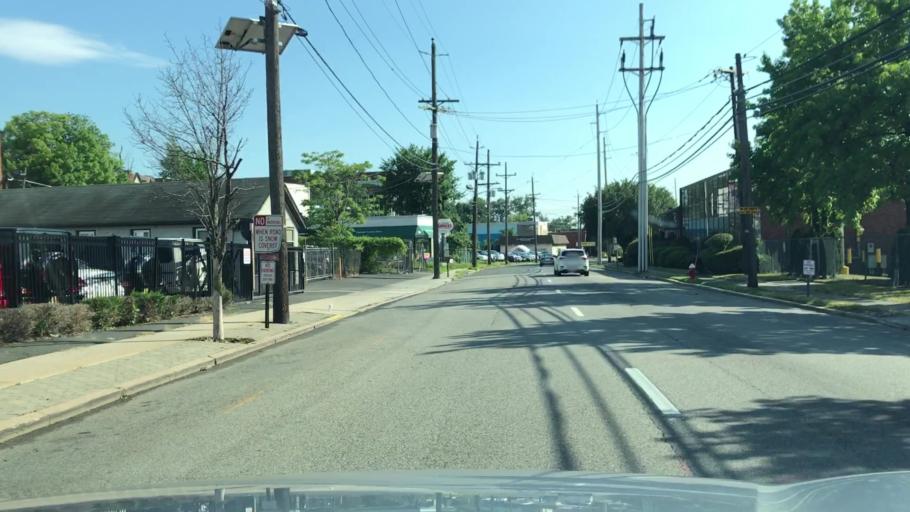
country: US
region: New Jersey
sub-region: Bergen County
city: Englewood
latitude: 40.8920
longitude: -73.9754
